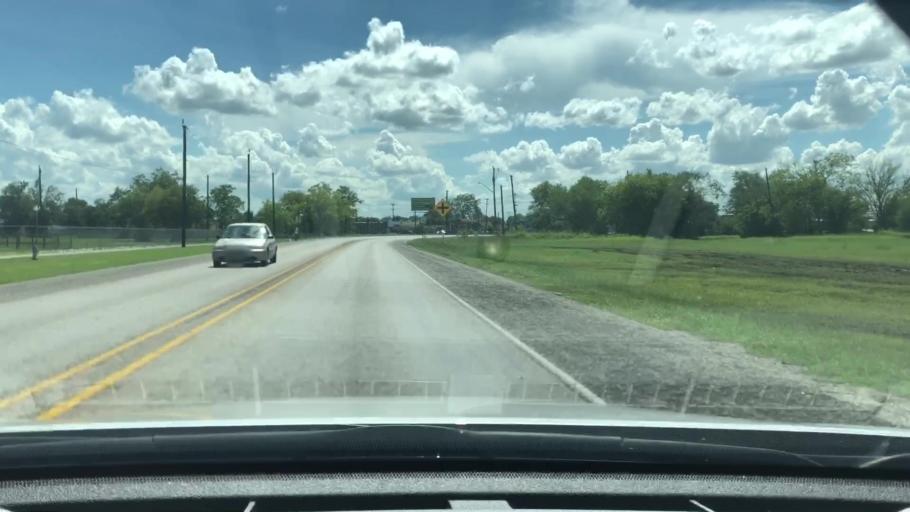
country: US
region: Texas
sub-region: Bexar County
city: Converse
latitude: 29.5204
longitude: -98.3141
